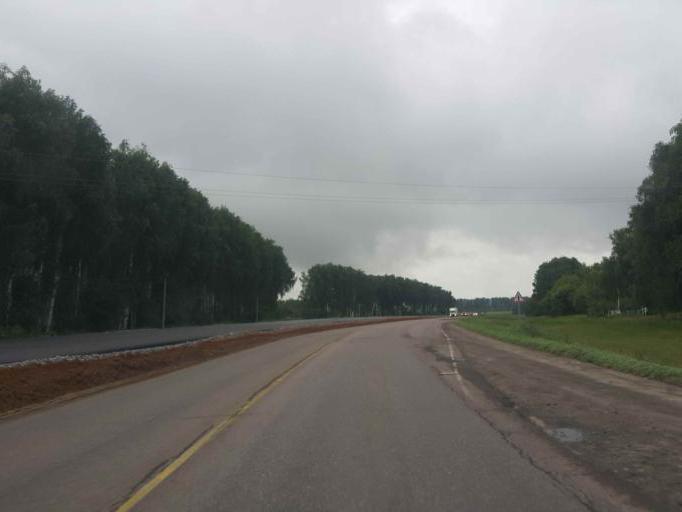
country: RU
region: Tambov
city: Selezni
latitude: 52.7697
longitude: 41.0561
